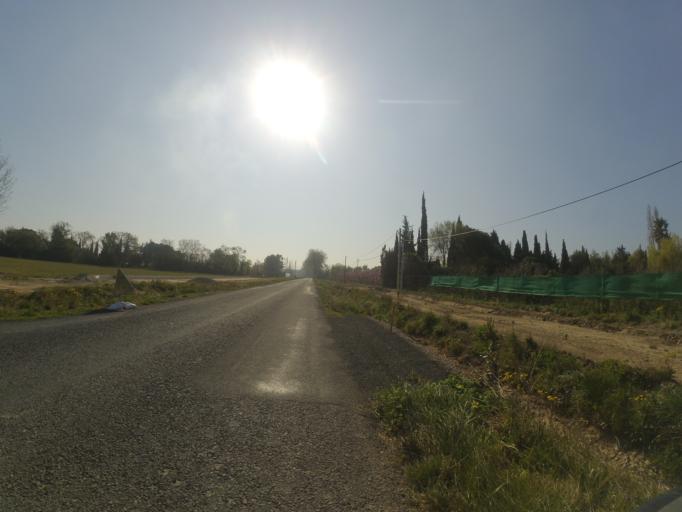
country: FR
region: Languedoc-Roussillon
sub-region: Departement des Pyrenees-Orientales
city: Thuir
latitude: 42.6450
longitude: 2.7390
